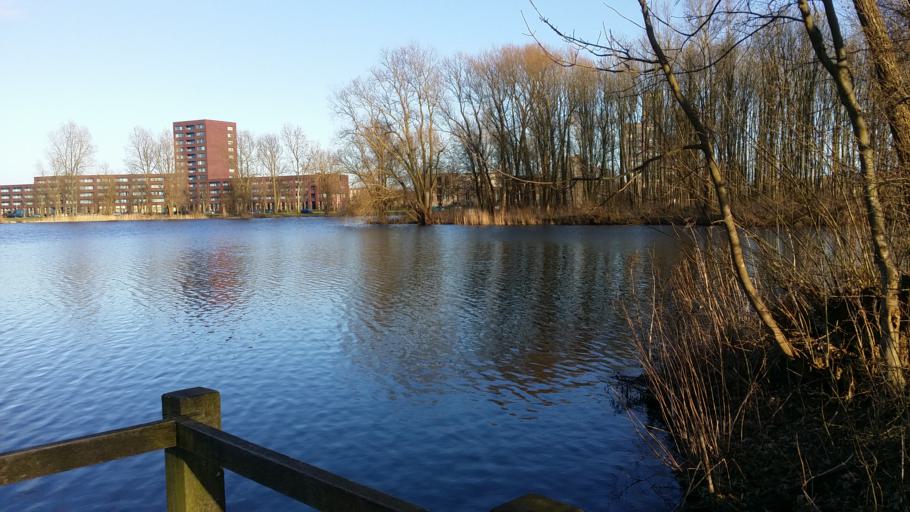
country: NL
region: South Holland
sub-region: Gemeente Den Haag
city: Ypenburg
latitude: 52.0481
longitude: 4.3697
